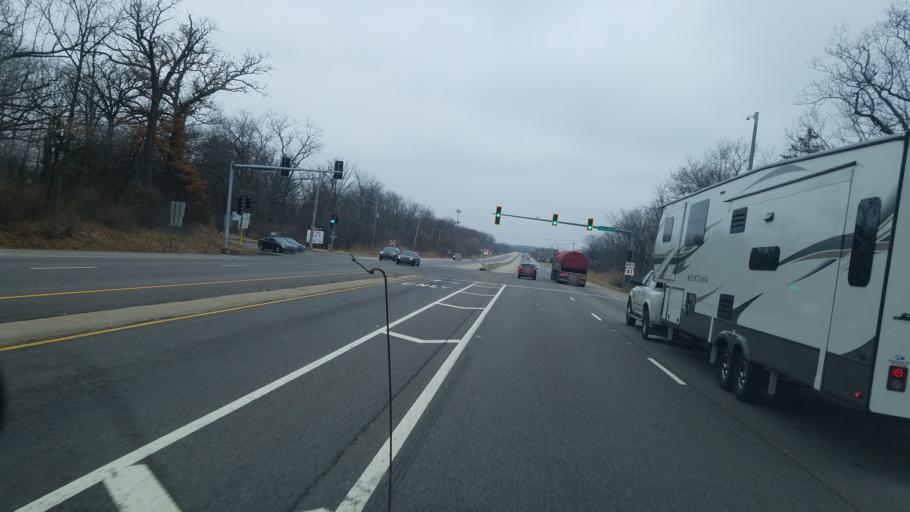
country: US
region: Illinois
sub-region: Lake County
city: Gurnee
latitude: 42.3924
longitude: -87.9261
